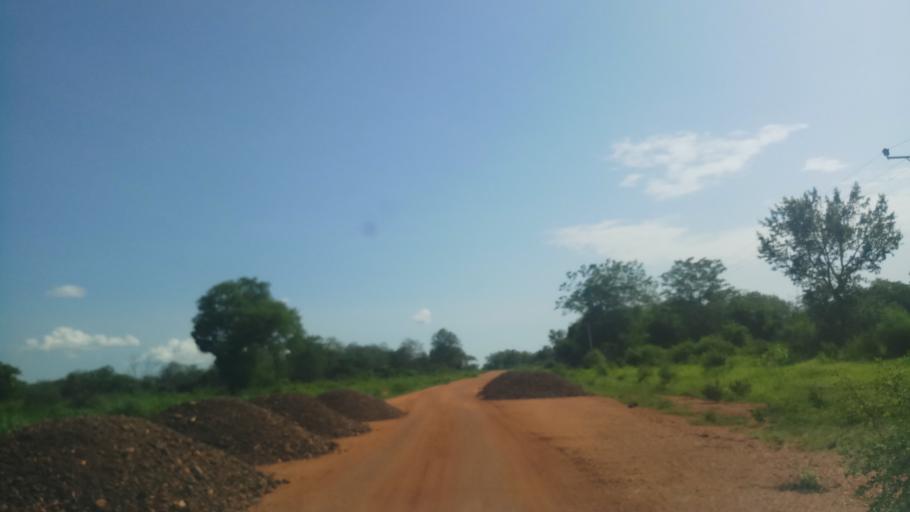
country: ET
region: Gambela
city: Gambela
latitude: 8.1339
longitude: 34.3984
